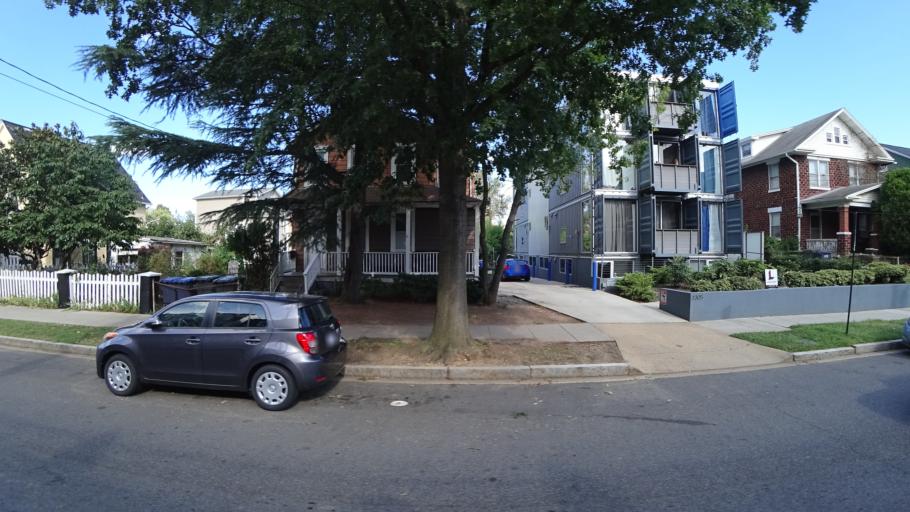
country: US
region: Maryland
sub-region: Prince George's County
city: Mount Rainier
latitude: 38.9309
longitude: -76.9962
